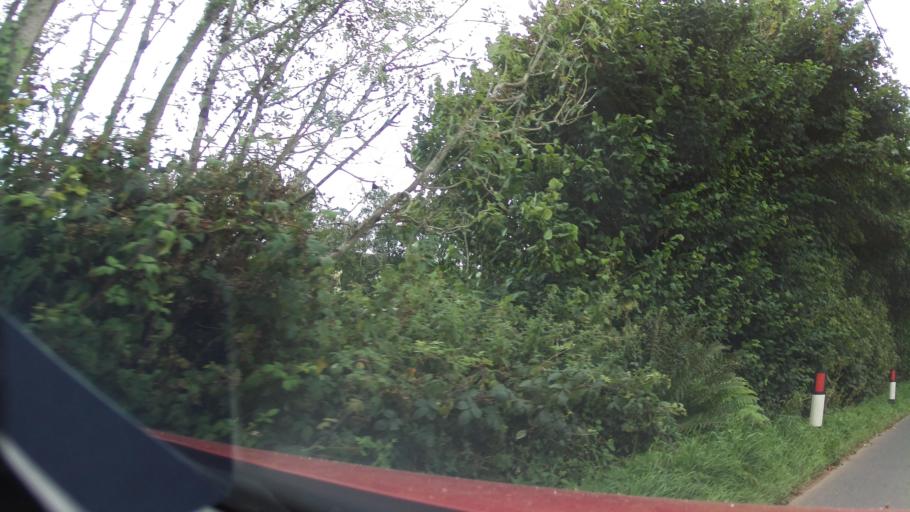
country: GB
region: England
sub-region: Devon
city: South Brent
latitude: 50.4016
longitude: -3.8279
